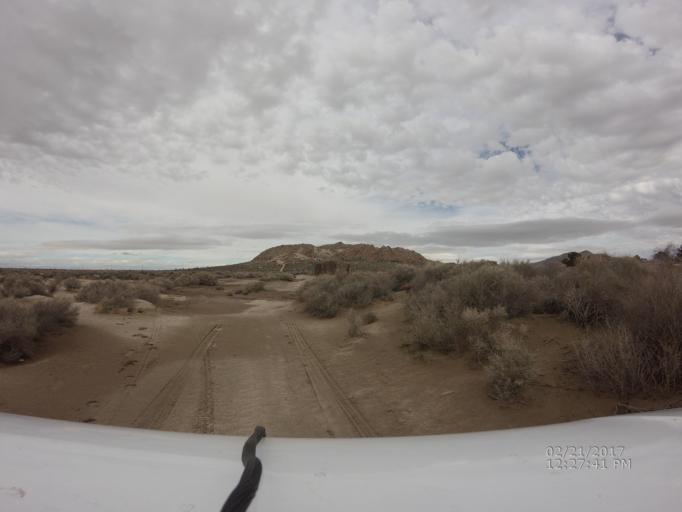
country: US
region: California
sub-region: Los Angeles County
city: Lake Los Angeles
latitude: 34.6411
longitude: -117.8539
